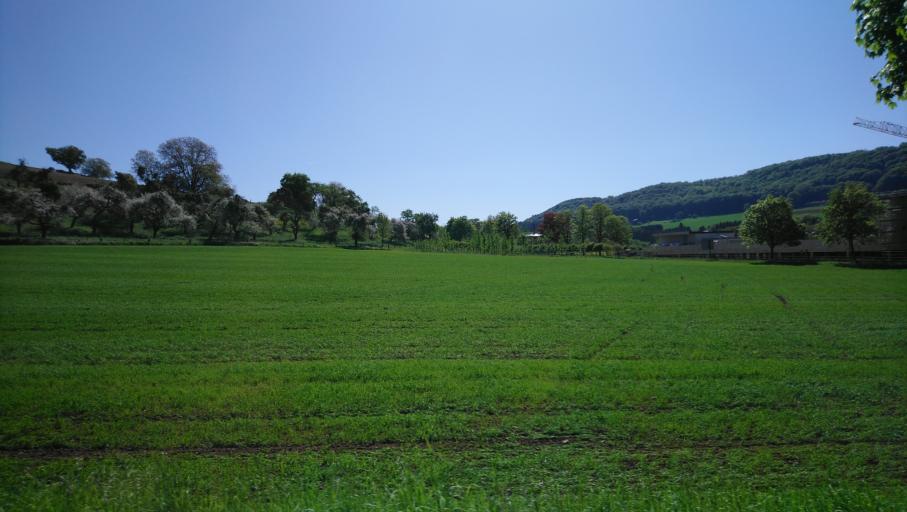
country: LU
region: Diekirch
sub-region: Canton de Vianden
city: Tandel
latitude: 49.8731
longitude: 6.1902
